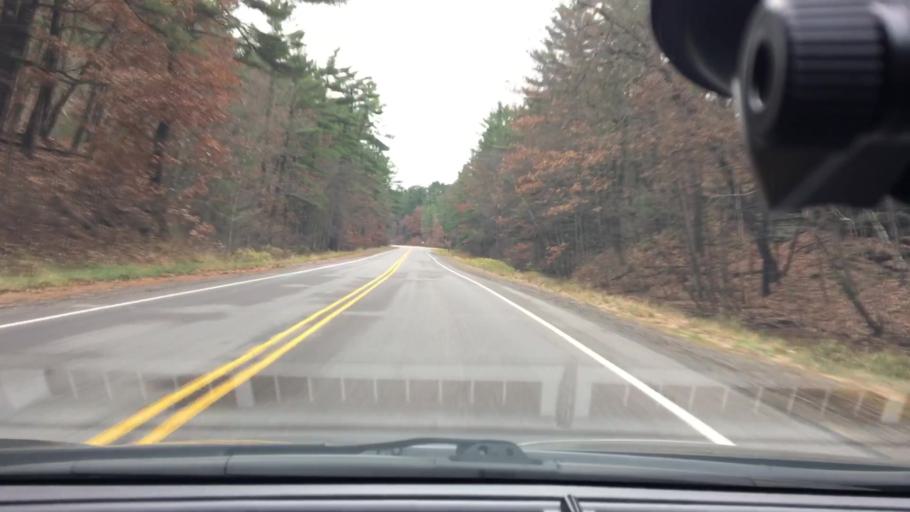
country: US
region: Wisconsin
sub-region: Columbia County
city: Wisconsin Dells
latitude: 43.6437
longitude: -89.8046
